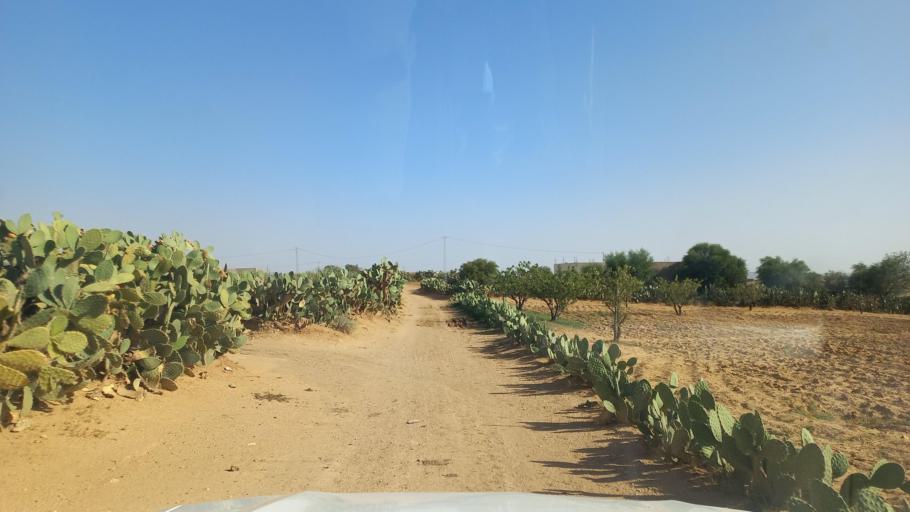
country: TN
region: Al Qasrayn
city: Sbiba
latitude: 35.3204
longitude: 9.0209
